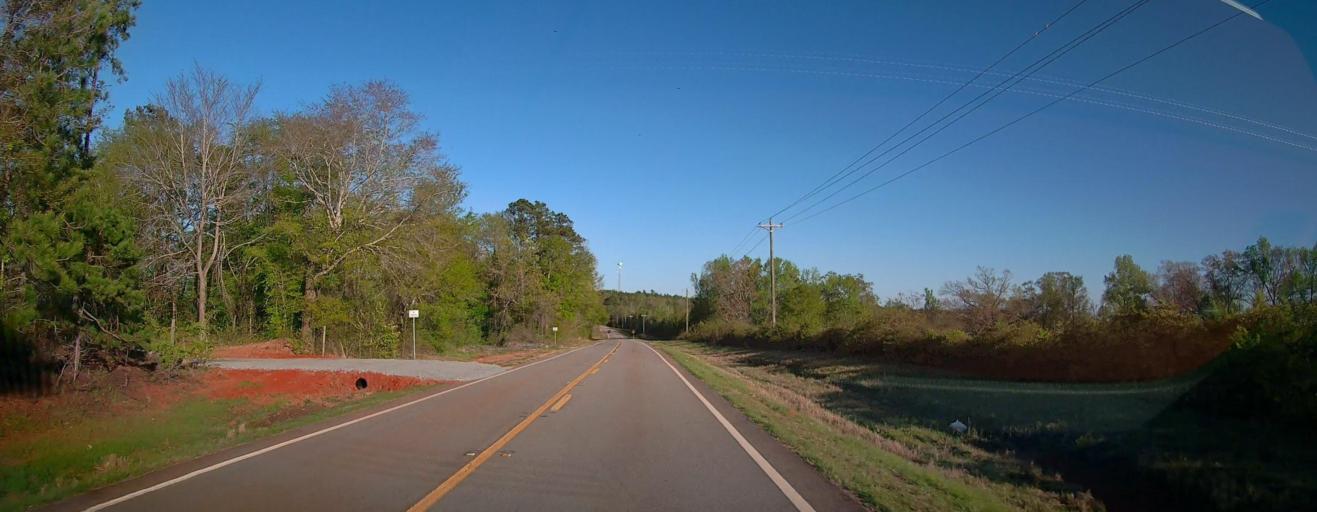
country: US
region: Georgia
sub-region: Wilkinson County
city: Irwinton
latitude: 32.8609
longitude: -83.0825
